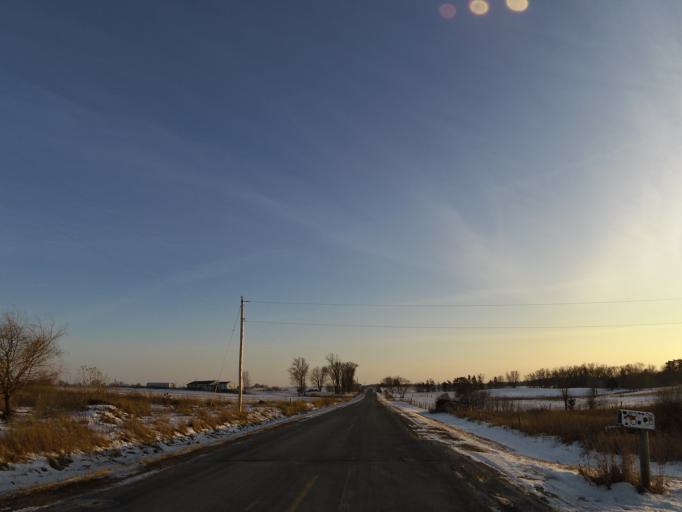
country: US
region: Wisconsin
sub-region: Pierce County
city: River Falls
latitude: 44.9242
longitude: -92.5989
